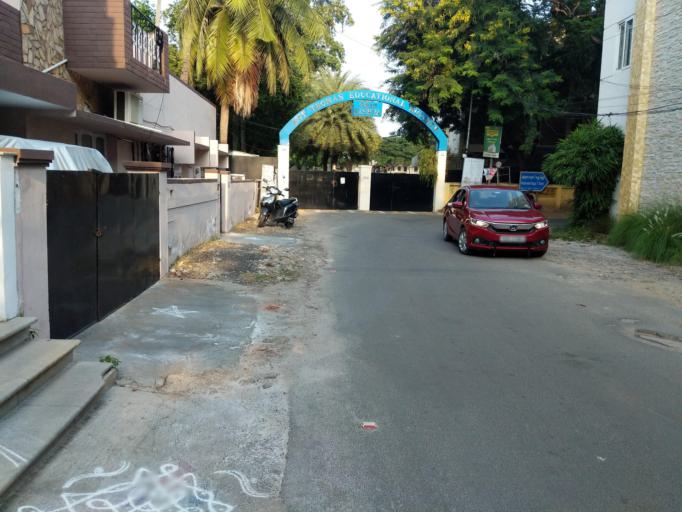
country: IN
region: Tamil Nadu
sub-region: Chennai
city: Gandhi Nagar
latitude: 13.0052
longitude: 80.2586
